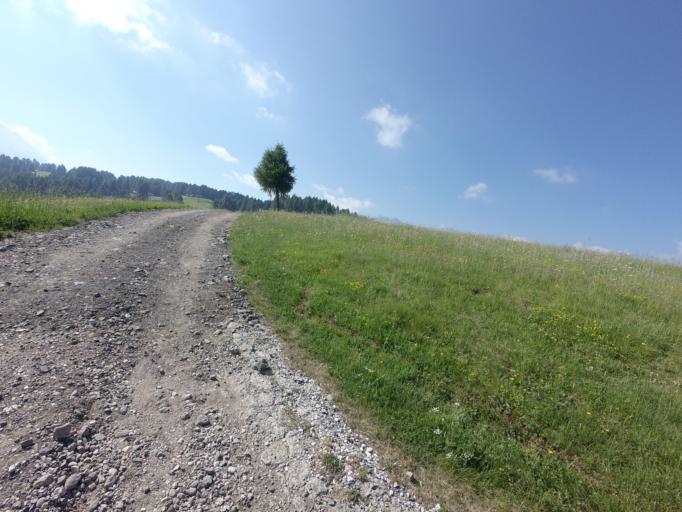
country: IT
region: Trentino-Alto Adige
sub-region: Bolzano
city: Ortisei
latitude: 46.5442
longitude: 11.6328
